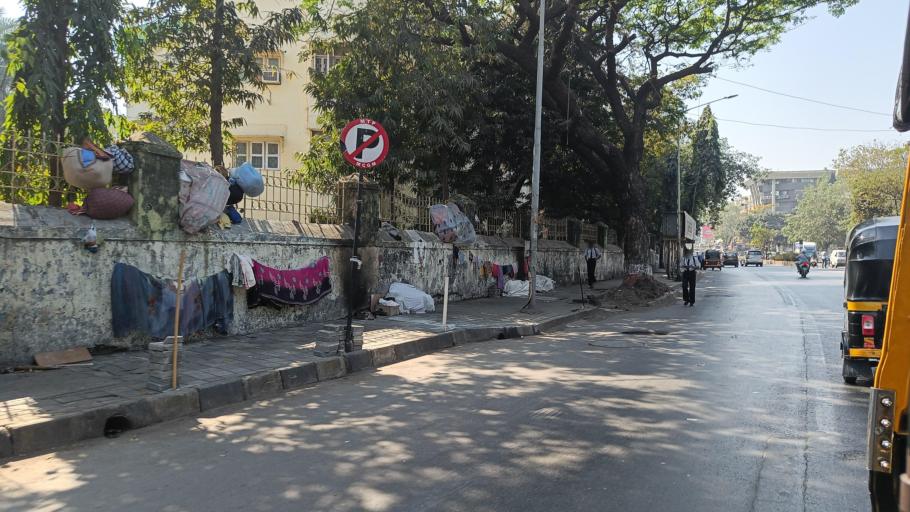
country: IN
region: Maharashtra
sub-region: Mumbai Suburban
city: Mumbai
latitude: 19.0916
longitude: 72.8386
